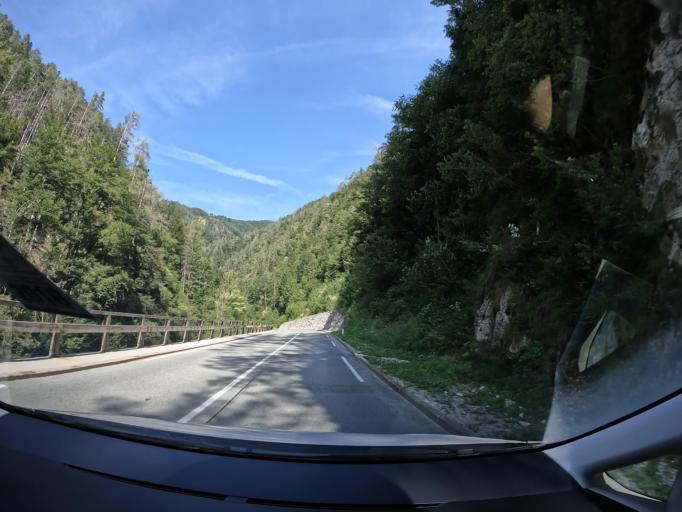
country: SI
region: Trzic
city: Trzic
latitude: 46.4189
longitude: 14.2895
